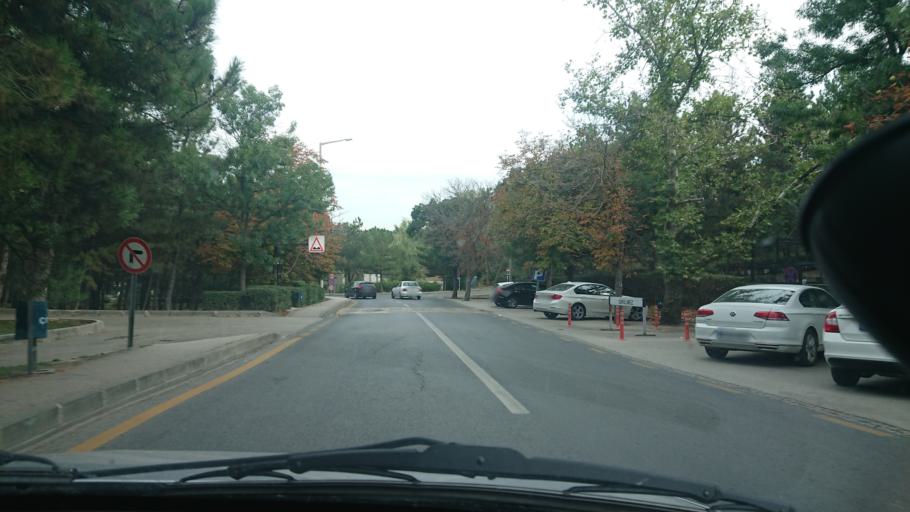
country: TR
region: Ankara
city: Ankara
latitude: 39.8922
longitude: 32.7891
